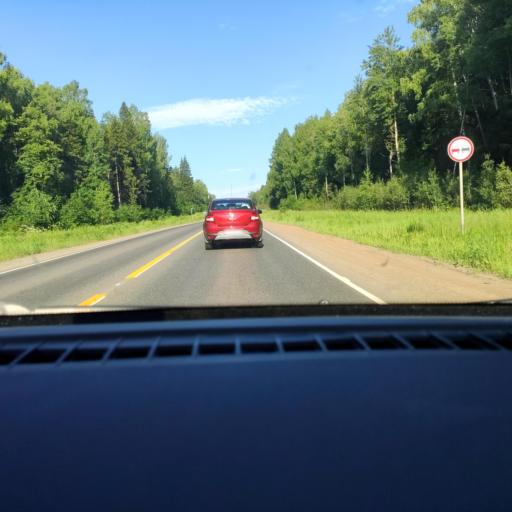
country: RU
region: Udmurtiya
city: Khokhryaki
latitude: 56.9160
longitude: 53.4353
